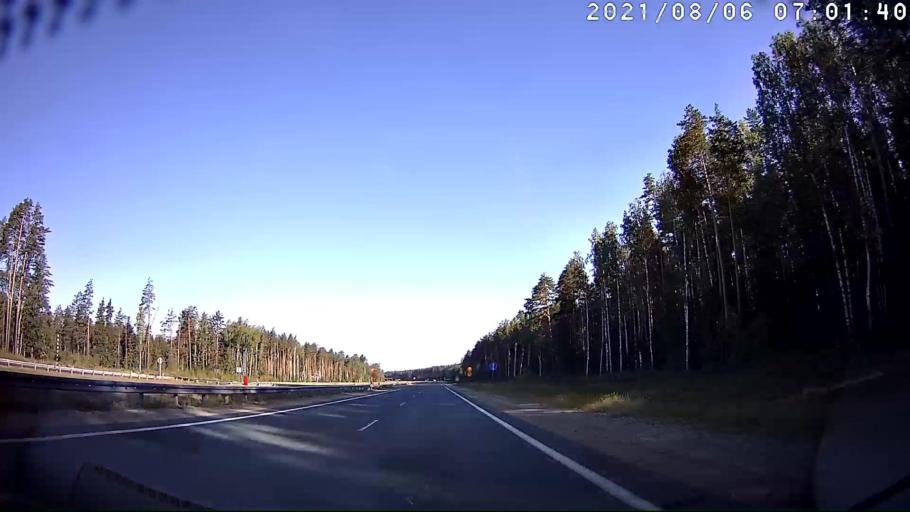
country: RU
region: Mariy-El
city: Surok
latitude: 56.5256
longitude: 48.0072
